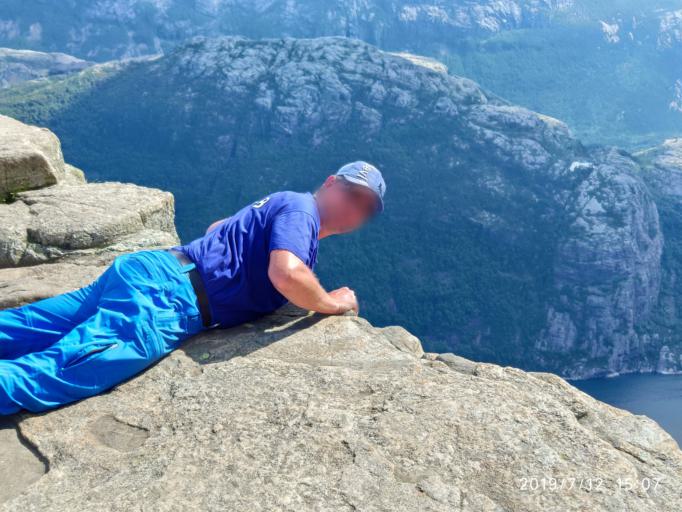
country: NO
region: Rogaland
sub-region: Forsand
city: Forsand
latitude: 58.9861
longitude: 6.1885
